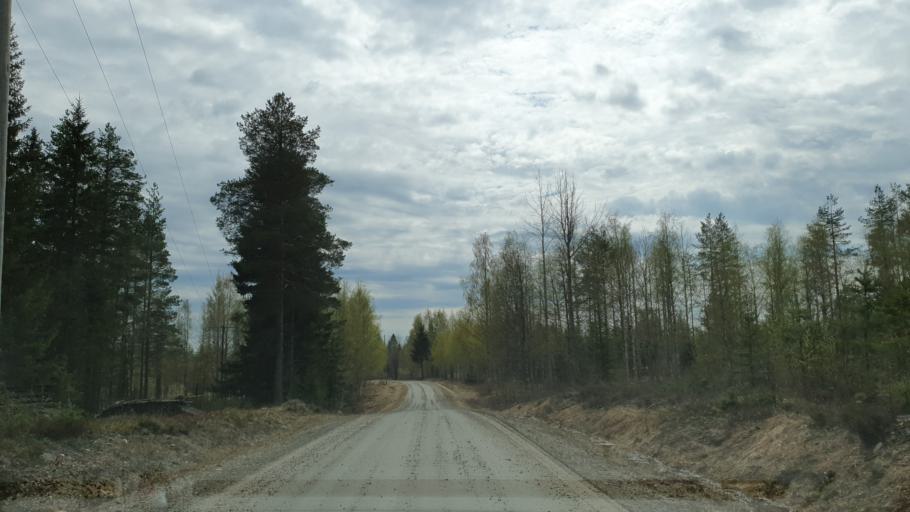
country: FI
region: Kainuu
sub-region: Kehys-Kainuu
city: Kuhmo
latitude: 64.1366
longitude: 29.9703
